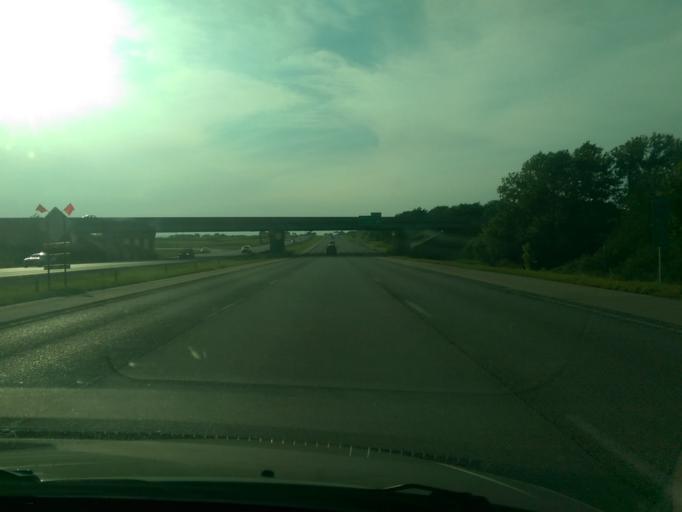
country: US
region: Missouri
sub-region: Platte County
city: Platte City
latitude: 39.3282
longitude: -94.7099
